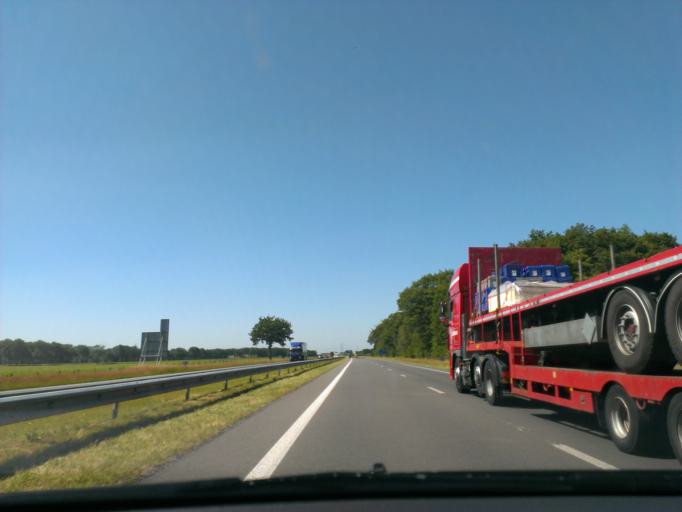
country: NL
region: Drenthe
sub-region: Gemeente Coevorden
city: Sleen
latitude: 52.7417
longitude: 6.8103
